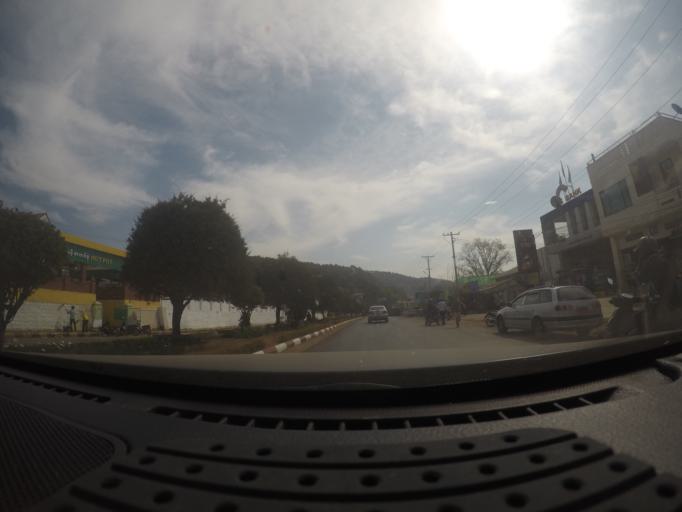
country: MM
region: Mandalay
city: Yamethin
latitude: 20.6362
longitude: 96.5676
